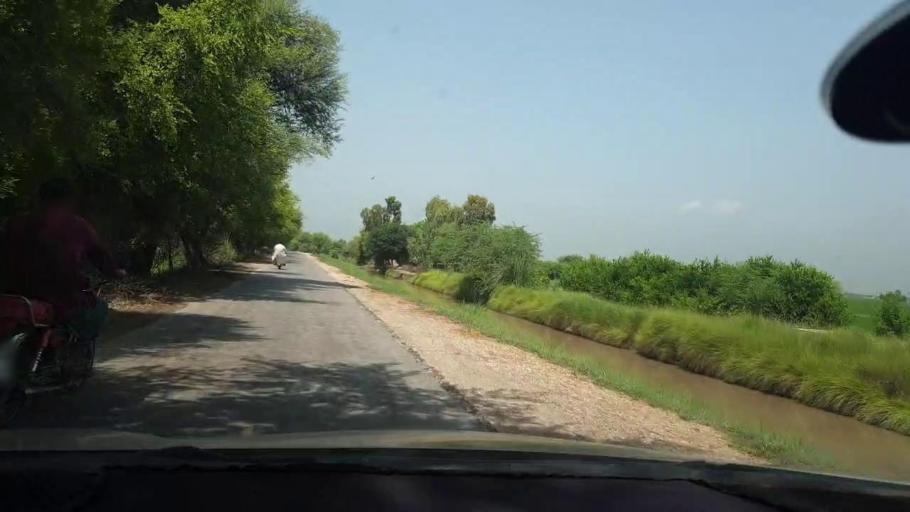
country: PK
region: Sindh
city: Kambar
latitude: 27.6444
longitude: 67.9723
